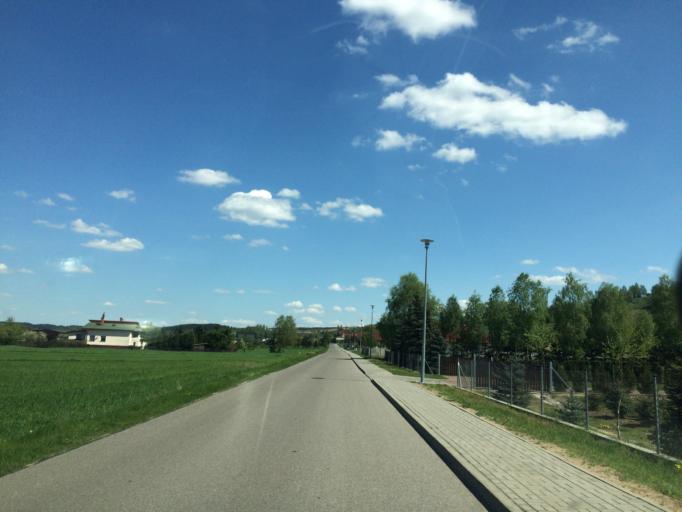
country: PL
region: Warmian-Masurian Voivodeship
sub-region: Powiat nowomiejski
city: Kurzetnik
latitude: 53.3969
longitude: 19.5617
